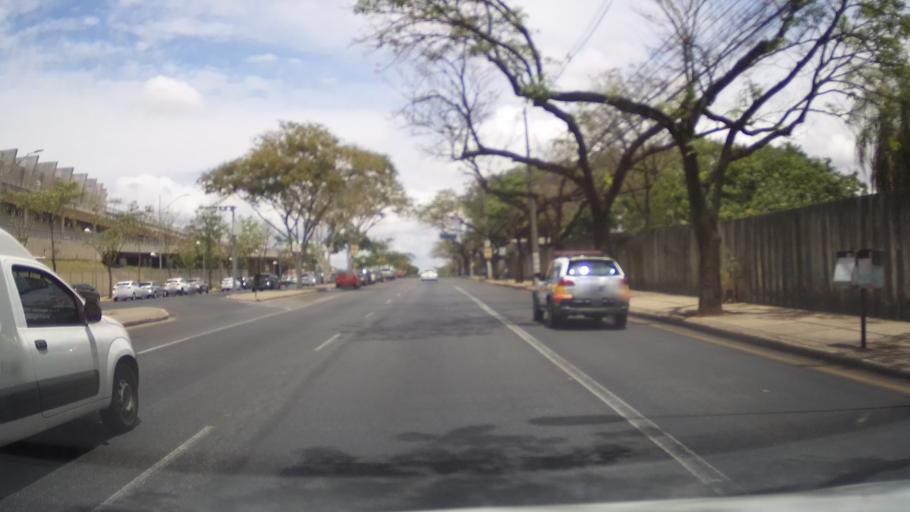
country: BR
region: Minas Gerais
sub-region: Belo Horizonte
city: Belo Horizonte
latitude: -19.8653
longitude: -43.9734
